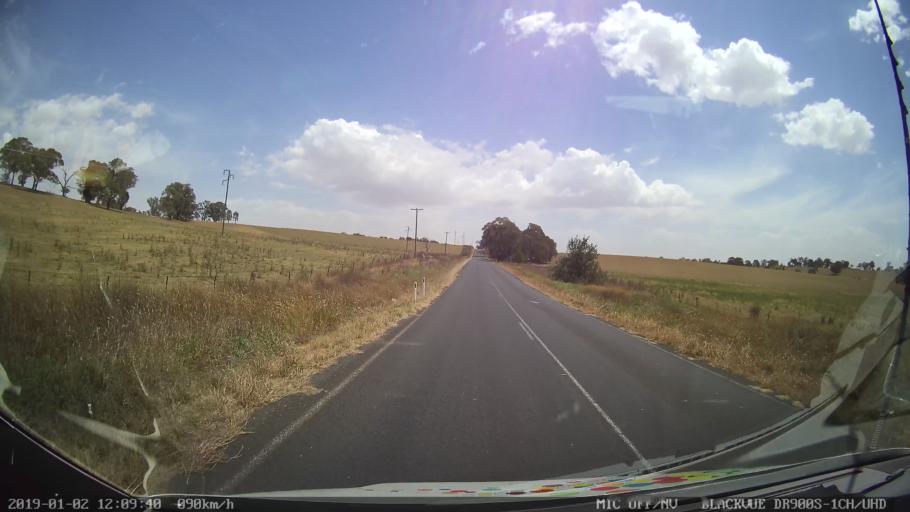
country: AU
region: New South Wales
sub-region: Young
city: Young
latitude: -34.4694
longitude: 148.2687
